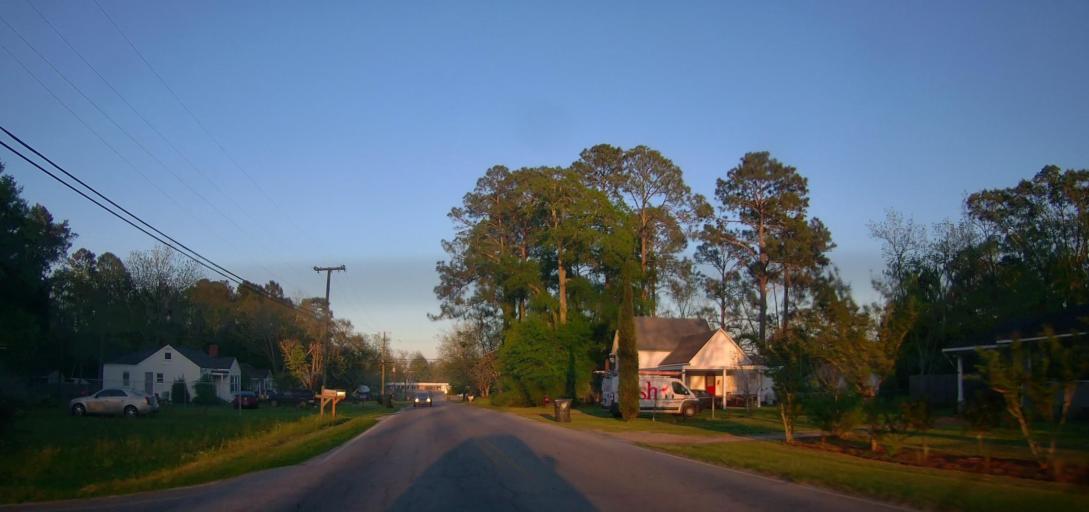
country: US
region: Georgia
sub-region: Ben Hill County
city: Fitzgerald
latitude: 31.7180
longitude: -83.2681
